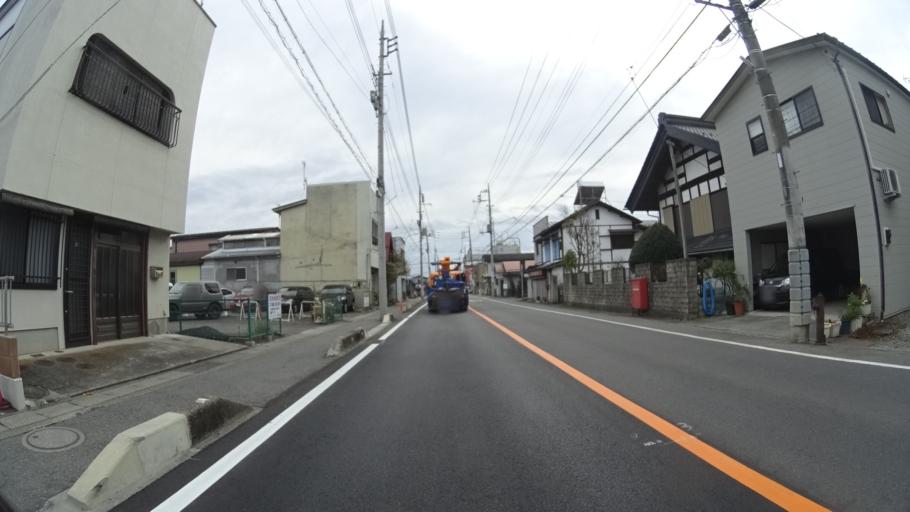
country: JP
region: Gunma
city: Numata
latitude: 36.6420
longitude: 139.0431
